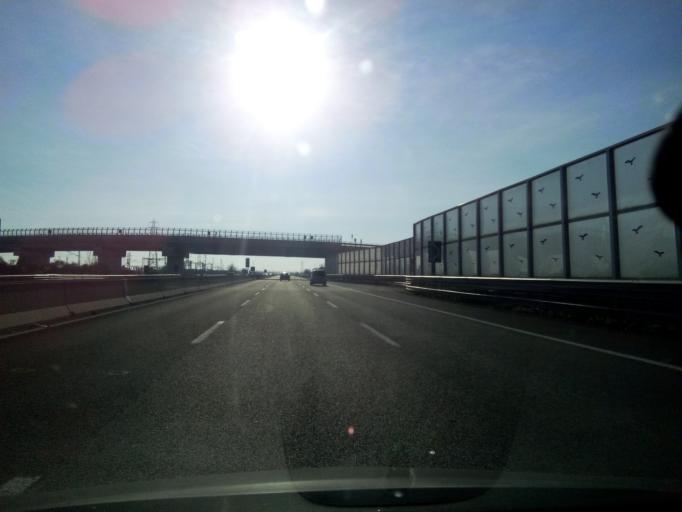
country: IT
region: Emilia-Romagna
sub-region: Provincia di Reggio Emilia
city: Massenzatico
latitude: 44.7140
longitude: 10.7017
